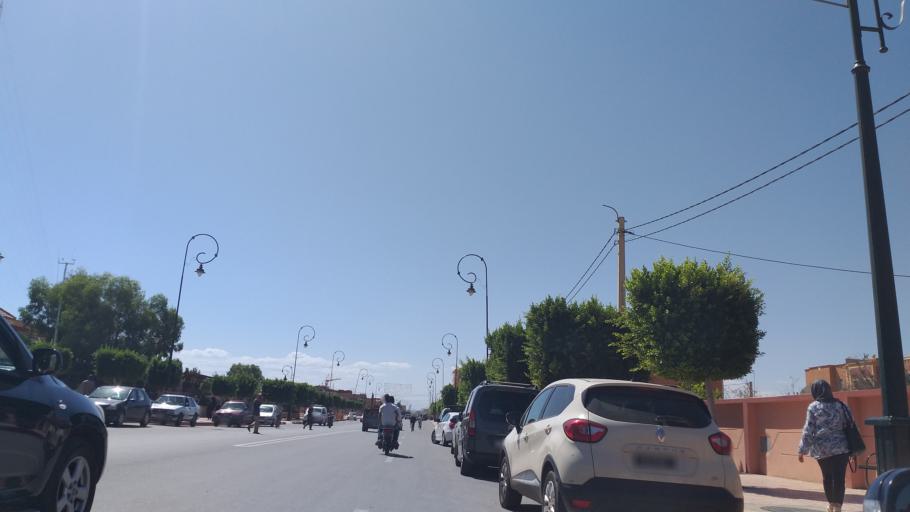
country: MA
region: Marrakech-Tensift-Al Haouz
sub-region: Chichaoua
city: Chichaoua
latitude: 31.5421
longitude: -8.7669
